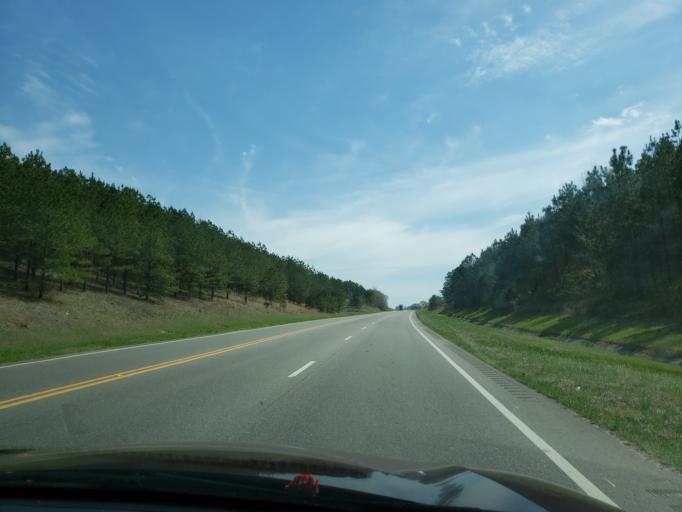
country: US
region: Alabama
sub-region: Autauga County
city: Prattville
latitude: 32.4326
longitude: -86.5605
